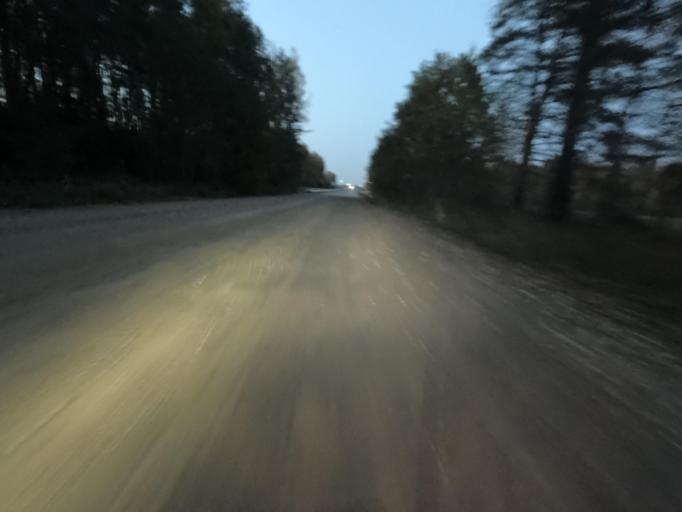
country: RU
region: Leningrad
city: Lyuban'
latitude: 59.1925
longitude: 31.2521
